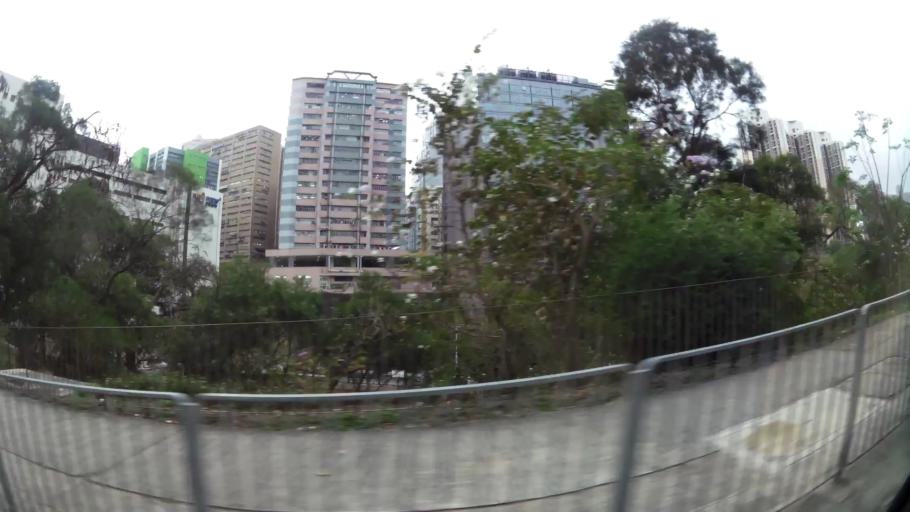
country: HK
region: Tsuen Wan
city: Tsuen Wan
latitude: 22.3717
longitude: 114.1301
